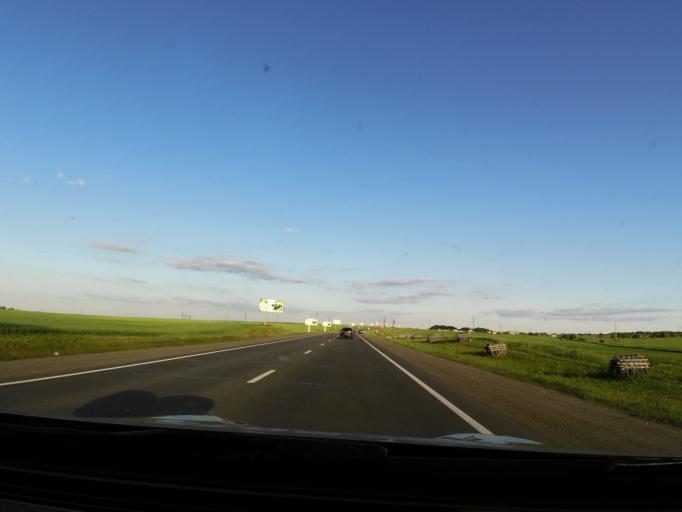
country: RU
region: Vologda
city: Vologda
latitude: 59.1667
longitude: 39.9167
